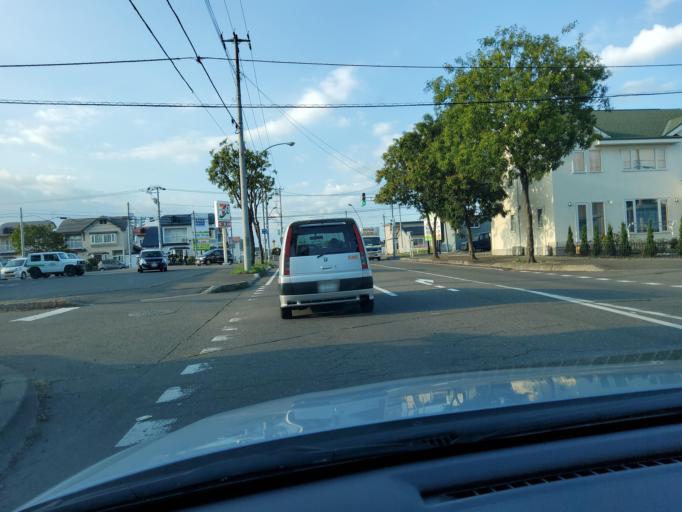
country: JP
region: Hokkaido
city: Obihiro
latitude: 42.9400
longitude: 143.1838
